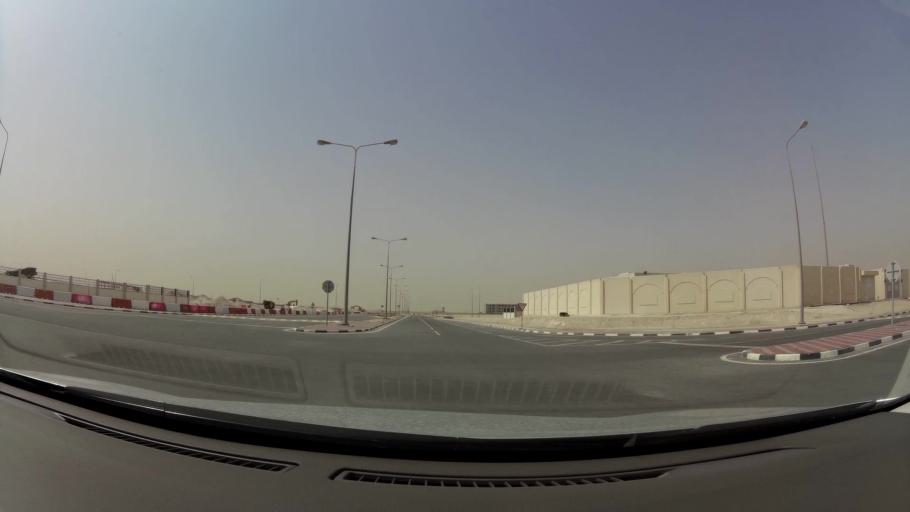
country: QA
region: Al Wakrah
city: Al Wukayr
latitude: 25.1488
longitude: 51.3970
